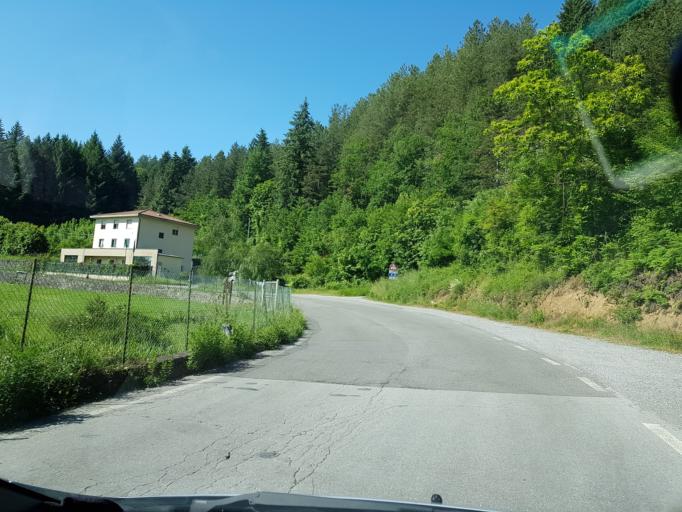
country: IT
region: Tuscany
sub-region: Provincia di Lucca
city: Camporgiano
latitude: 44.1663
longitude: 10.3274
